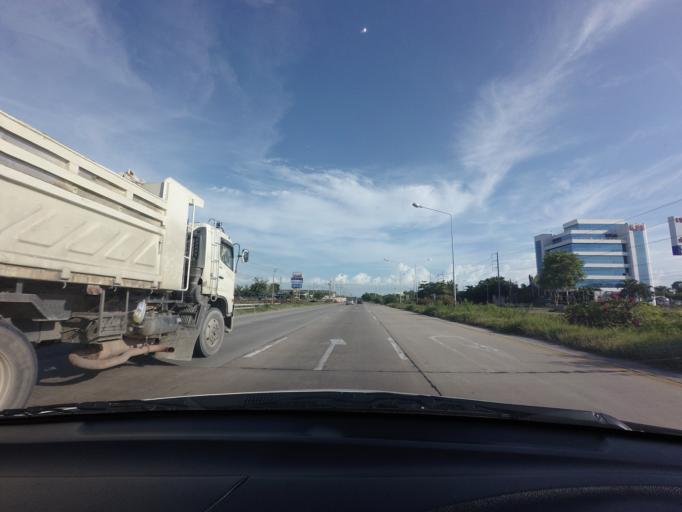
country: TH
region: Phra Nakhon Si Ayutthaya
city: Lat Bua Luang
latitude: 14.1260
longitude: 100.2895
